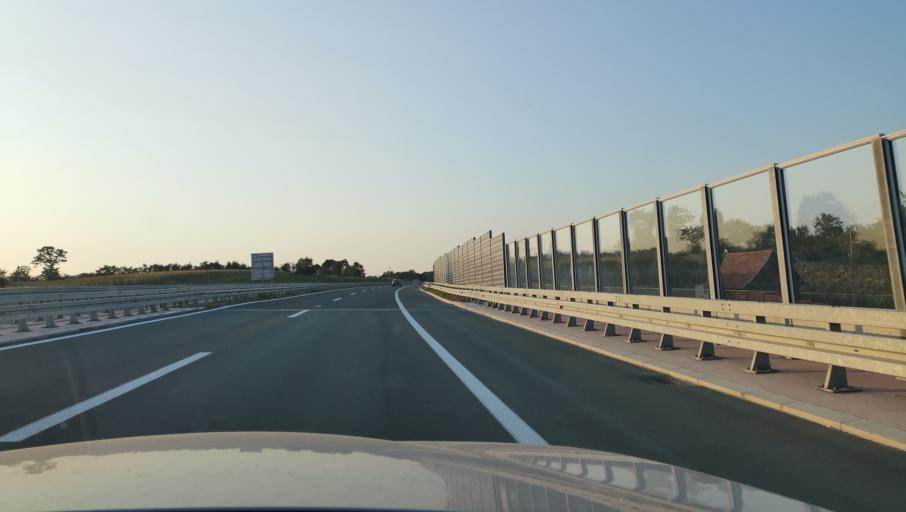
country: RS
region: Central Serbia
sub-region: Kolubarski Okrug
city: Lajkovac
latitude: 44.3637
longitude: 20.1214
